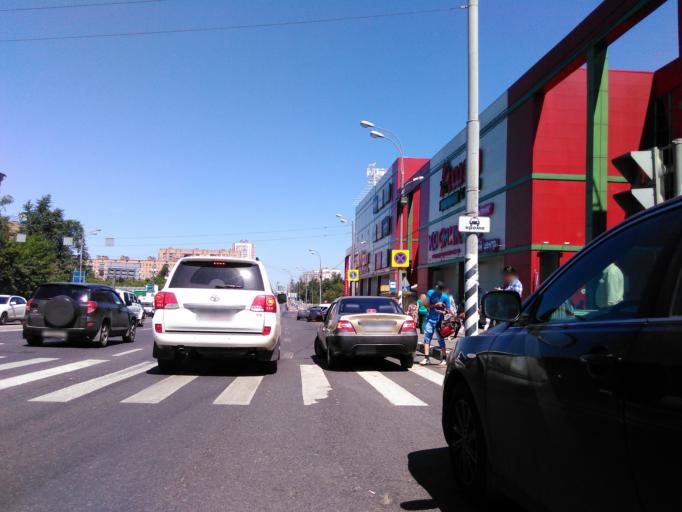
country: RU
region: Moscow
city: Novyye Cheremushki
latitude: 55.6875
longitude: 37.6034
